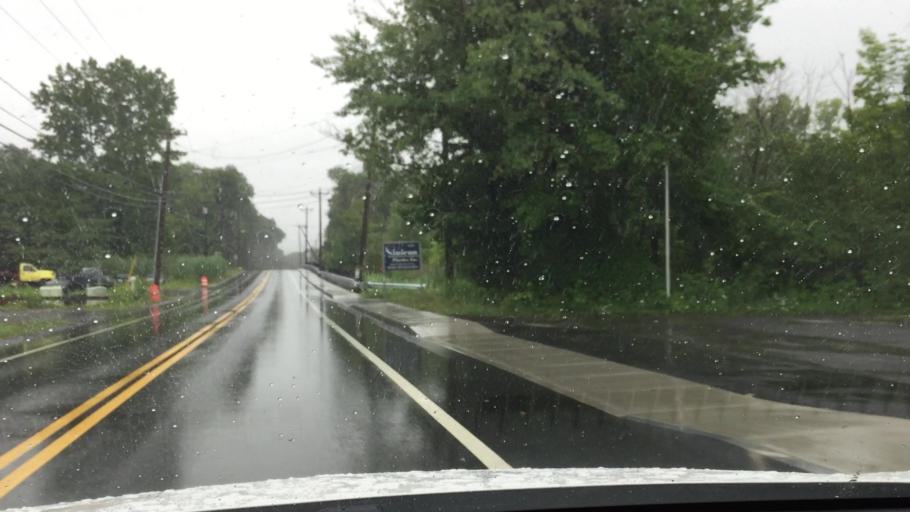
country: US
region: Massachusetts
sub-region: Berkshire County
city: Dalton
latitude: 42.4697
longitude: -73.1601
